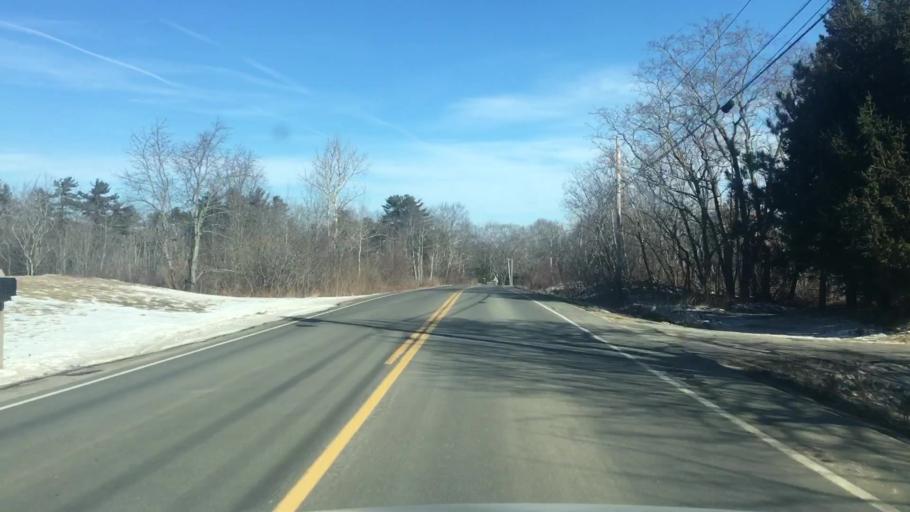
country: US
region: Maine
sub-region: Knox County
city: Rockland
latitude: 44.1365
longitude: -69.0968
